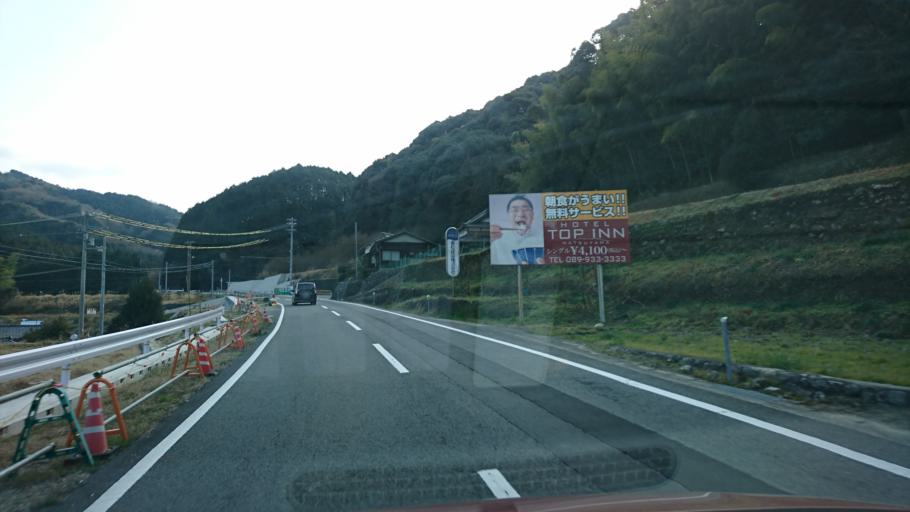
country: JP
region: Ehime
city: Hojo
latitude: 33.9866
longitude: 132.9081
